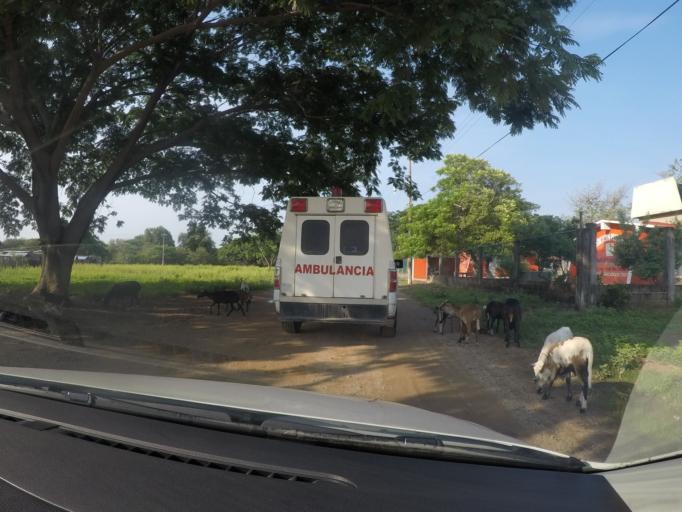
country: MX
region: Oaxaca
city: San Francisco Ixhuatan
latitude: 16.3359
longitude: -94.5213
